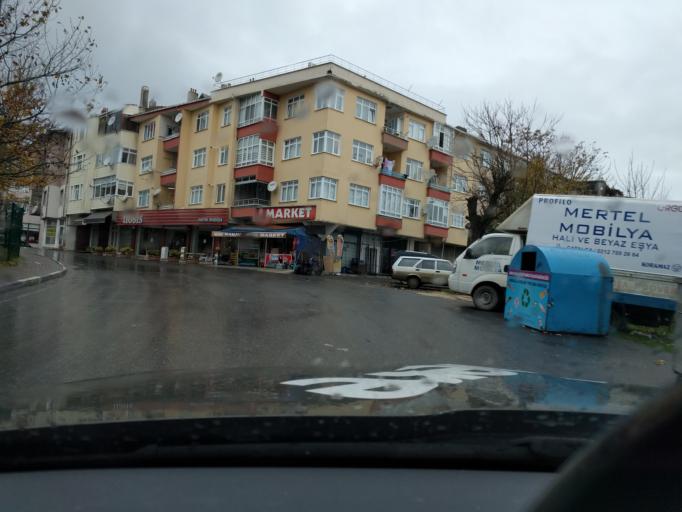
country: TR
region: Istanbul
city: Catalca
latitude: 41.1461
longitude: 28.4585
